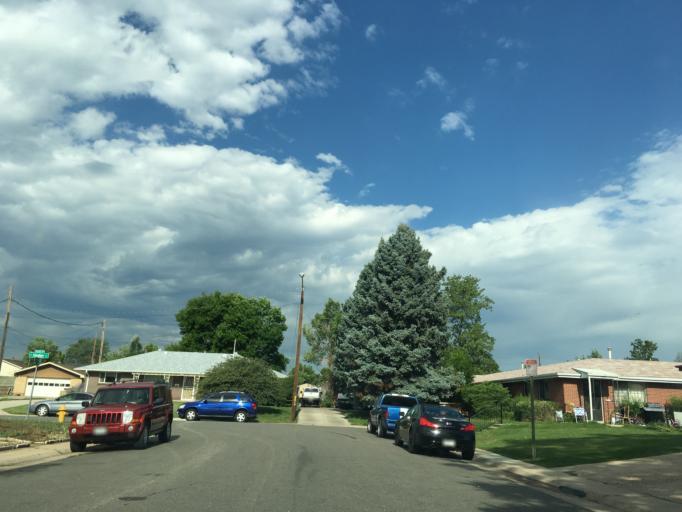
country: US
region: Colorado
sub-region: Arapahoe County
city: Sheridan
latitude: 39.6940
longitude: -105.0281
